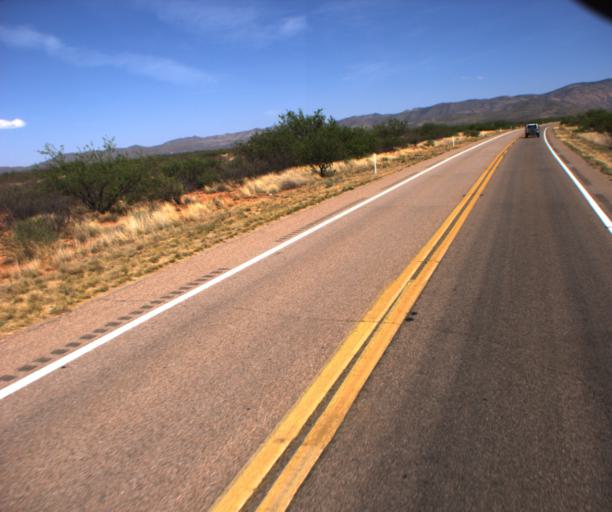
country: US
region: Arizona
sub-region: Cochise County
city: Sierra Vista Southeast
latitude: 31.5410
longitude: -110.0753
